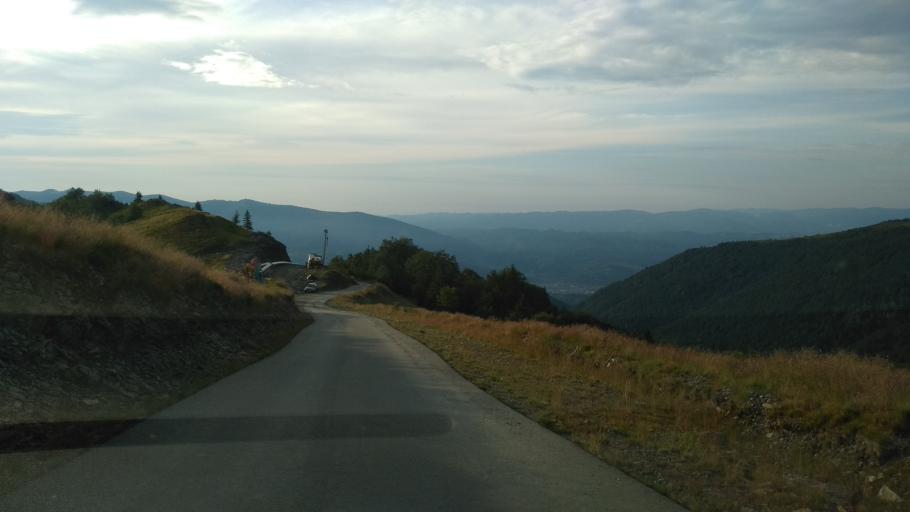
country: RO
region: Hunedoara
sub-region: Municipiul  Vulcan
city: Jiu-Paroseni
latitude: 45.3161
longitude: 23.3045
